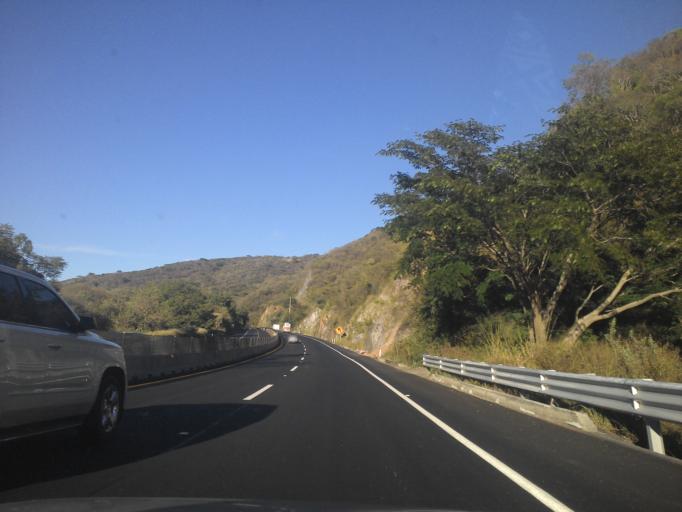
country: MX
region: Jalisco
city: Hostotipaquillo
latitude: 21.0009
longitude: -104.2057
